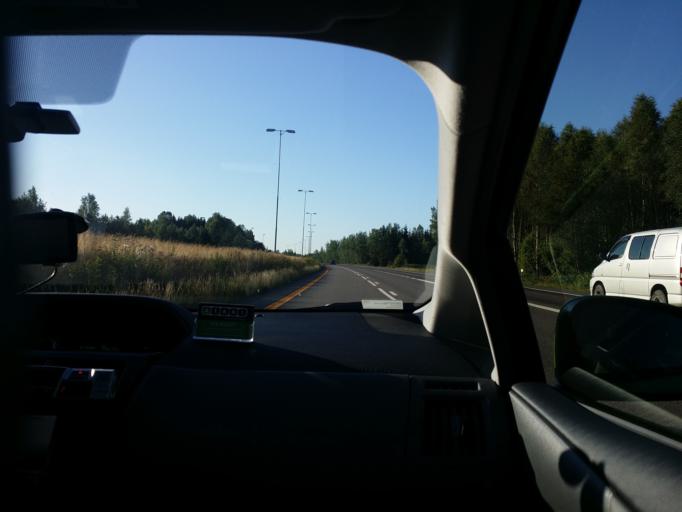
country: NO
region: Akershus
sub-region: Ullensaker
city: Jessheim
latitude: 60.1758
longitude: 11.0966
